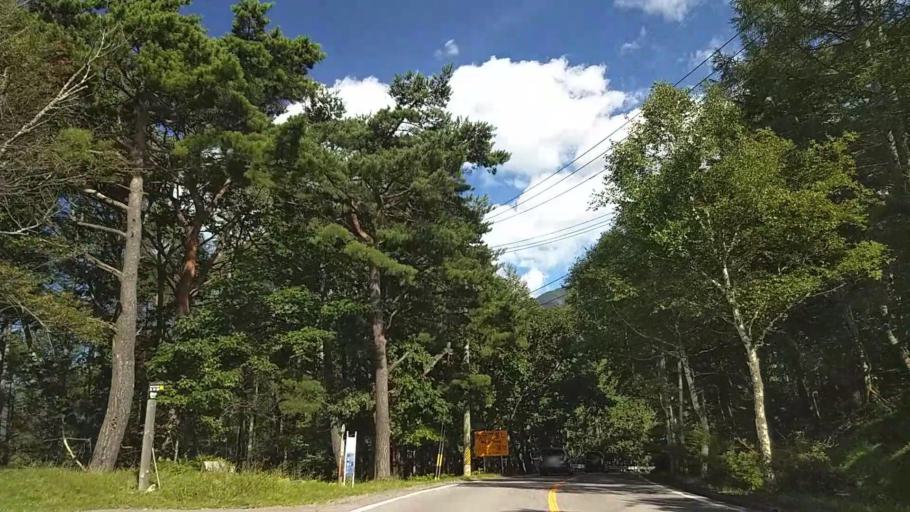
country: JP
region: Nagano
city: Chino
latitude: 36.1121
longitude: 138.2462
